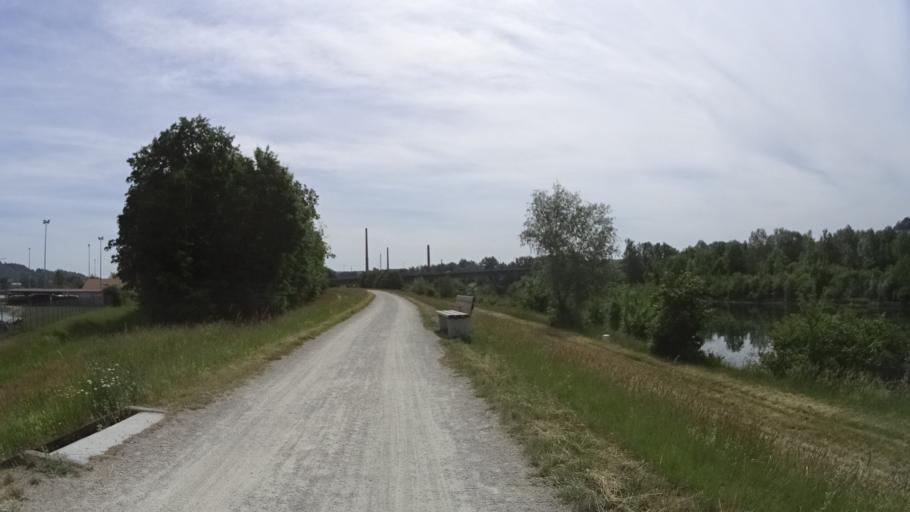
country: DE
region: Bavaria
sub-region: Lower Bavaria
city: Kelheim
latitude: 48.9114
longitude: 11.8881
